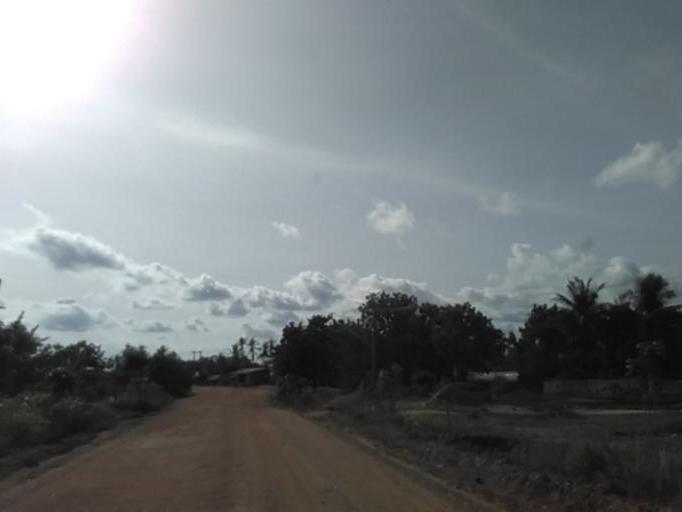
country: GH
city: Akropong
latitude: 6.0980
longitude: 0.2539
